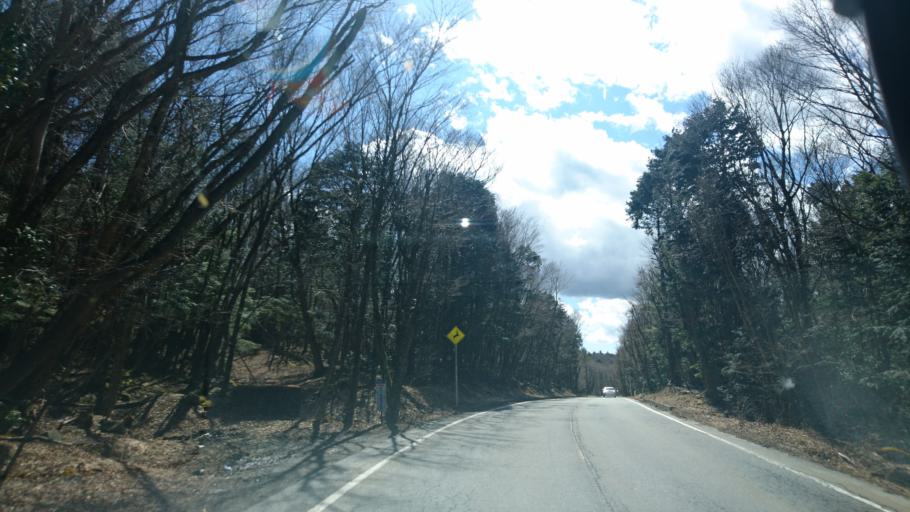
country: JP
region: Yamanashi
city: Fujikawaguchiko
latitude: 35.4485
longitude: 138.6418
